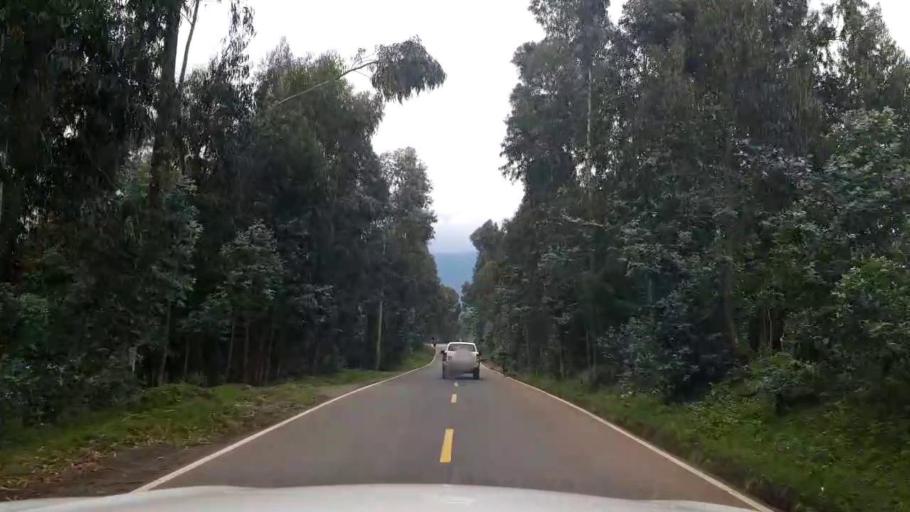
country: RW
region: Northern Province
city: Musanze
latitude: -1.4381
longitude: 29.5475
